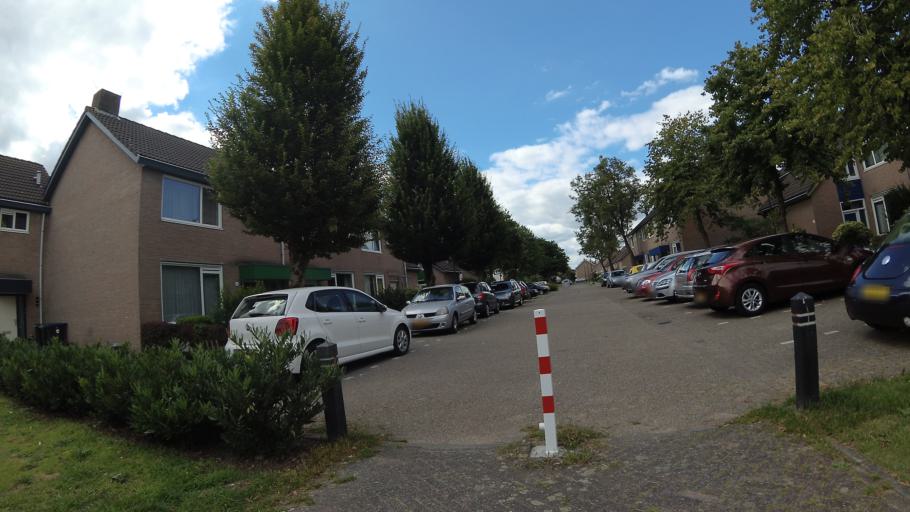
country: NL
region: North Brabant
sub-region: Gemeente Dongen
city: Dongen
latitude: 51.6350
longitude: 4.9445
